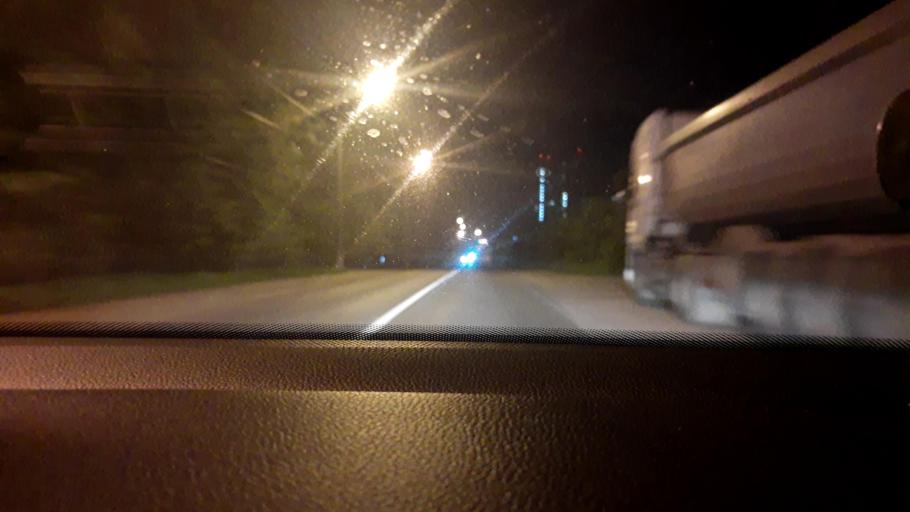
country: RU
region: Moskovskaya
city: Bolshevo
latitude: 55.9415
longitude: 37.8307
